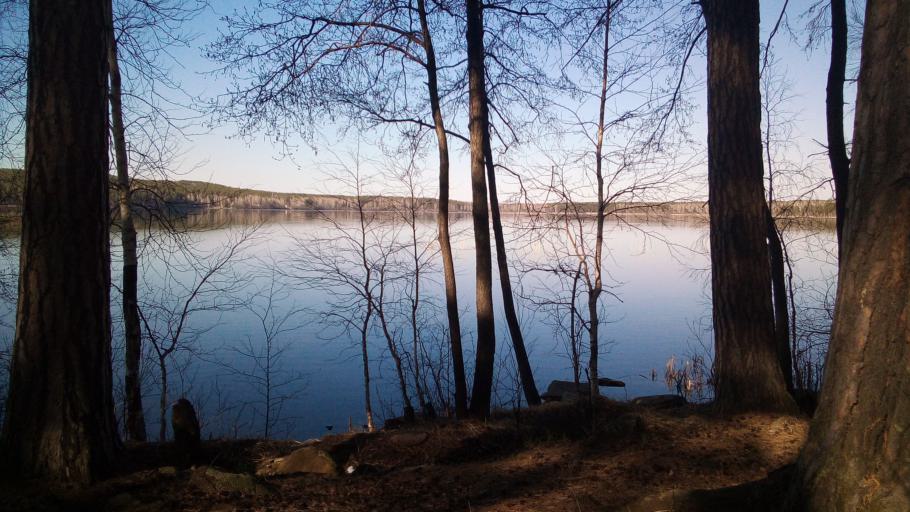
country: RU
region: Chelyabinsk
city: Chebarkul'
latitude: 55.1142
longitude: 60.3323
